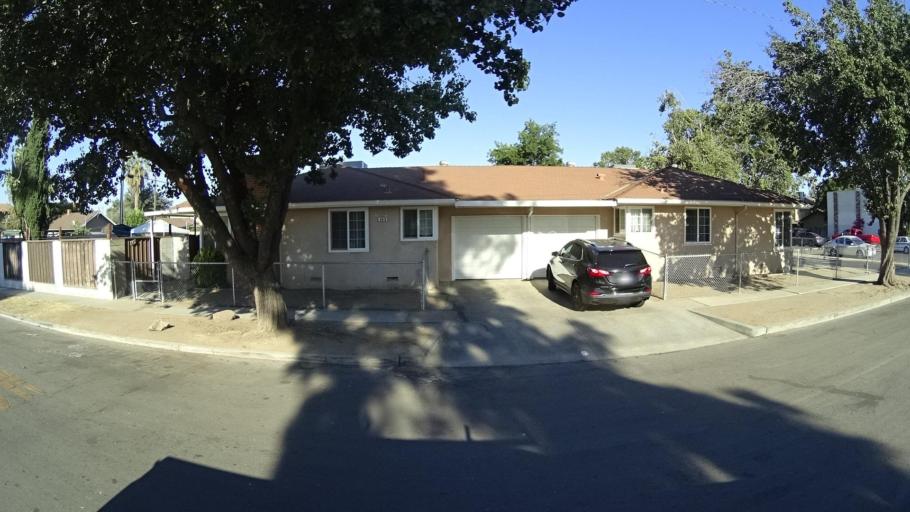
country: US
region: California
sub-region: Fresno County
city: Fresno
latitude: 36.7522
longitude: -119.7800
